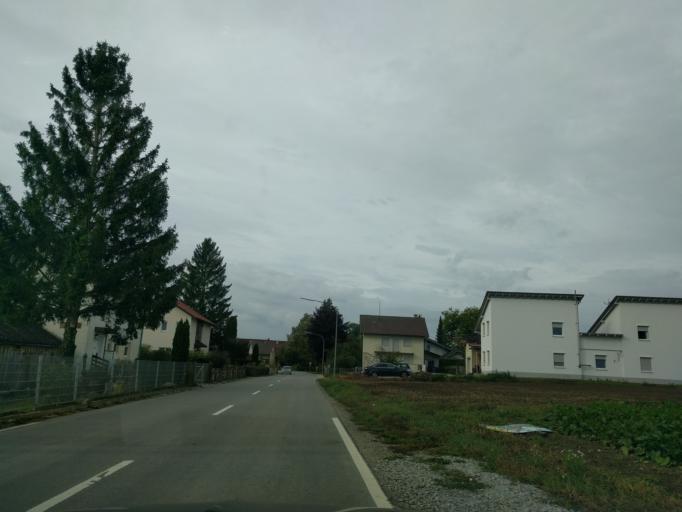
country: DE
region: Bavaria
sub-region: Lower Bavaria
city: Wallersdorf
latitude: 48.7402
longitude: 12.7566
